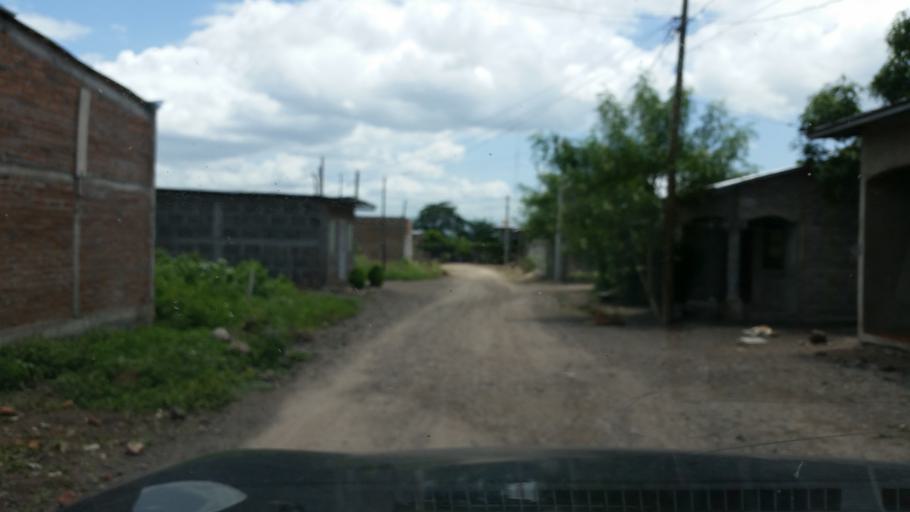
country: NI
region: Matagalpa
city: Ciudad Dario
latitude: 12.8645
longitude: -86.0905
